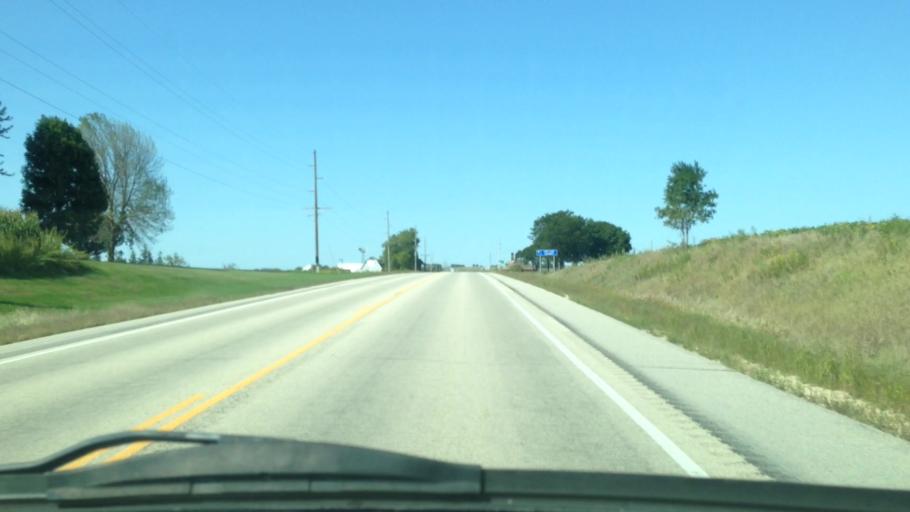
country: US
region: Minnesota
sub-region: Fillmore County
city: Rushford
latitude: 43.8715
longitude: -91.7396
